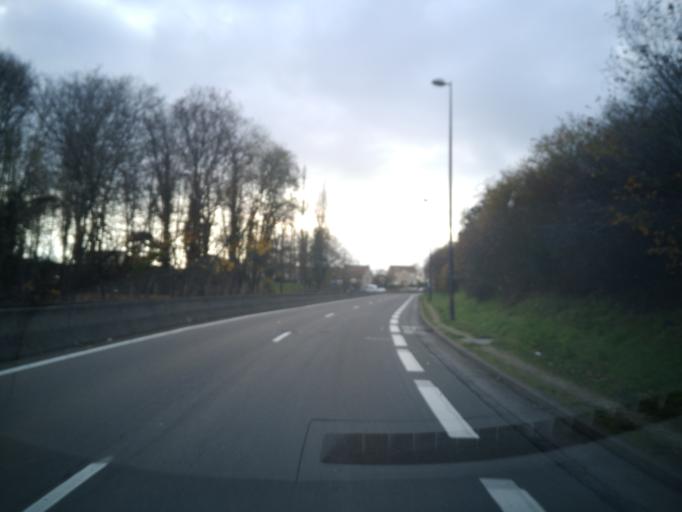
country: FR
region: Ile-de-France
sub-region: Departement des Yvelines
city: Guyancourt
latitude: 48.7767
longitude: 2.0946
